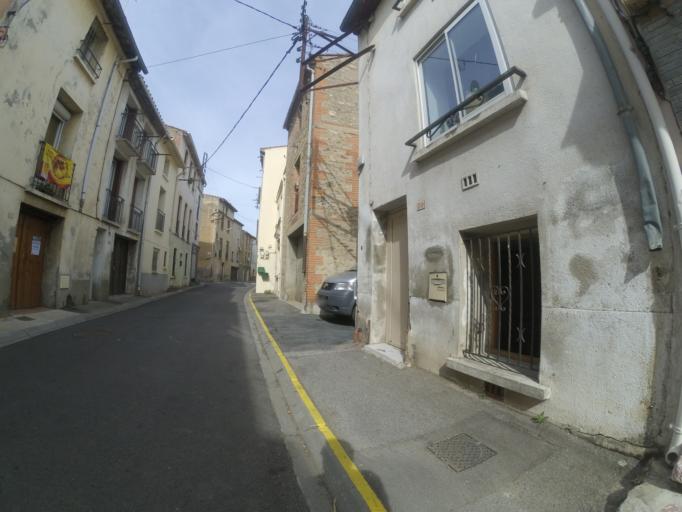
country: FR
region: Languedoc-Roussillon
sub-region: Departement des Pyrenees-Orientales
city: Millas
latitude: 42.6583
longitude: 2.6751
